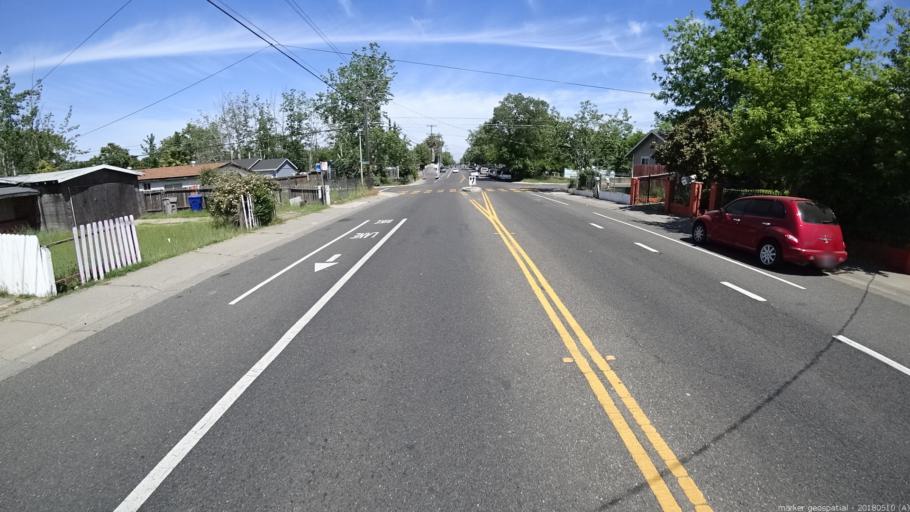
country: US
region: California
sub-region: Sacramento County
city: Rio Linda
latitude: 38.6368
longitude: -121.4530
